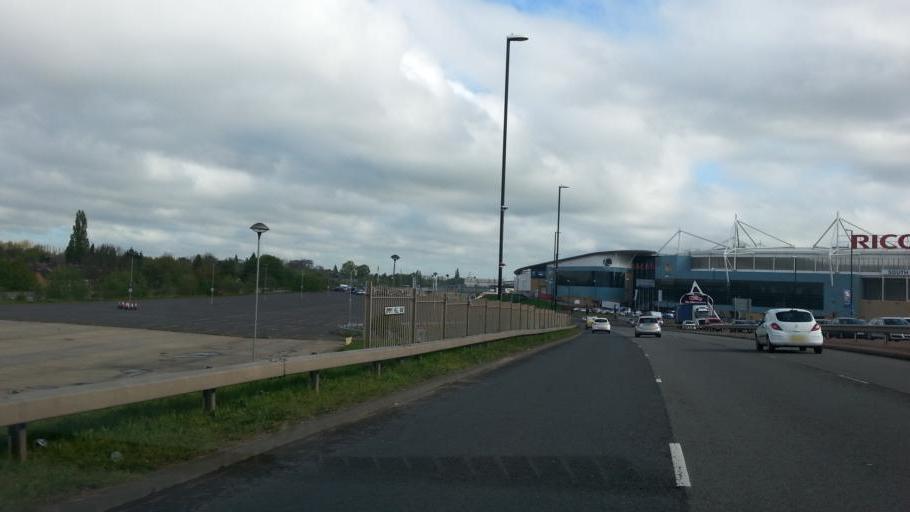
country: GB
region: England
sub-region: Warwickshire
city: Exhall
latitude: 52.4448
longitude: -1.4972
